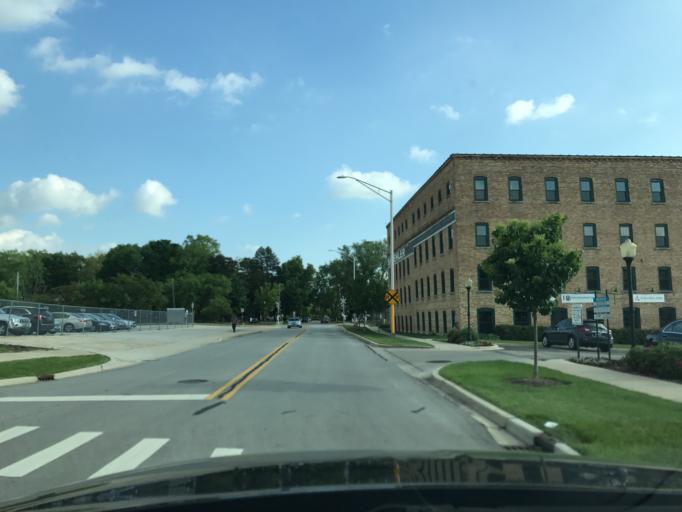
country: US
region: Illinois
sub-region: DuPage County
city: Naperville
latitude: 41.7807
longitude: -88.1421
